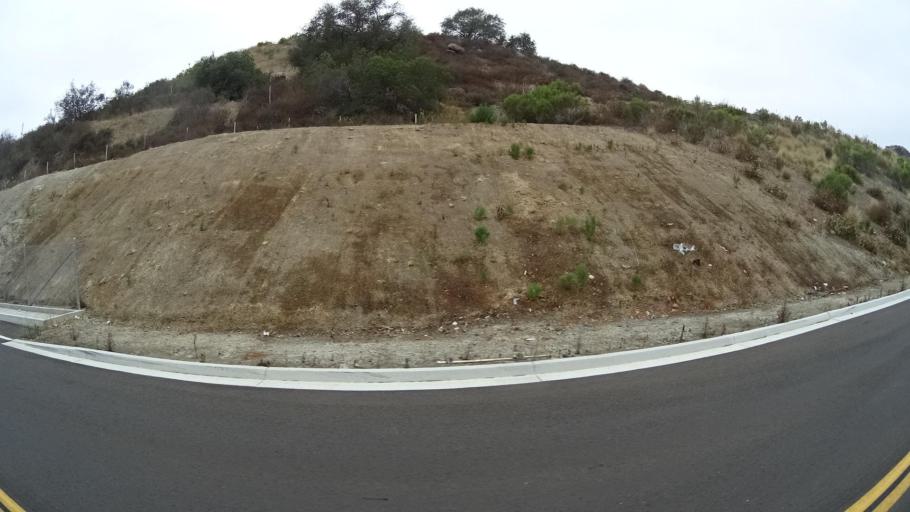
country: US
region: California
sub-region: San Diego County
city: Escondido
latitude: 33.1008
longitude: -117.1239
